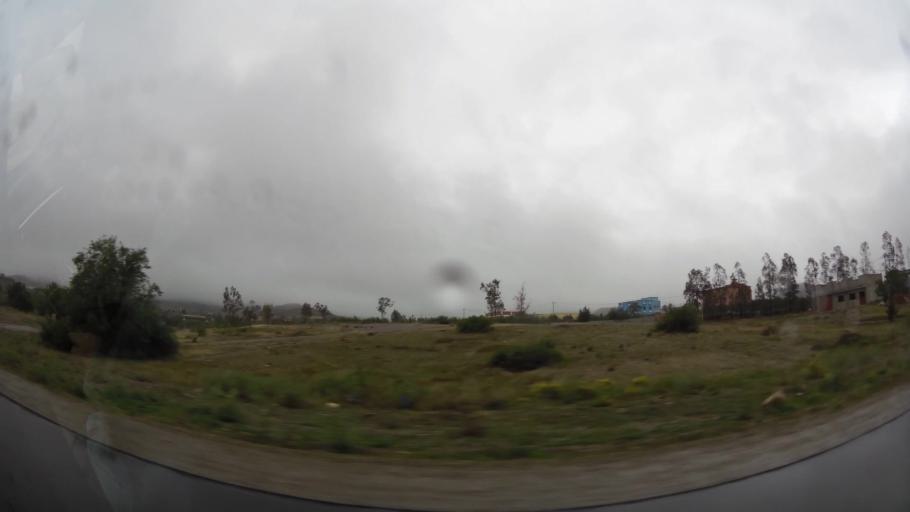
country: MA
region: Taza-Al Hoceima-Taounate
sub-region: Taza
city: Aknoul
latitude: 34.8222
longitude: -3.7248
